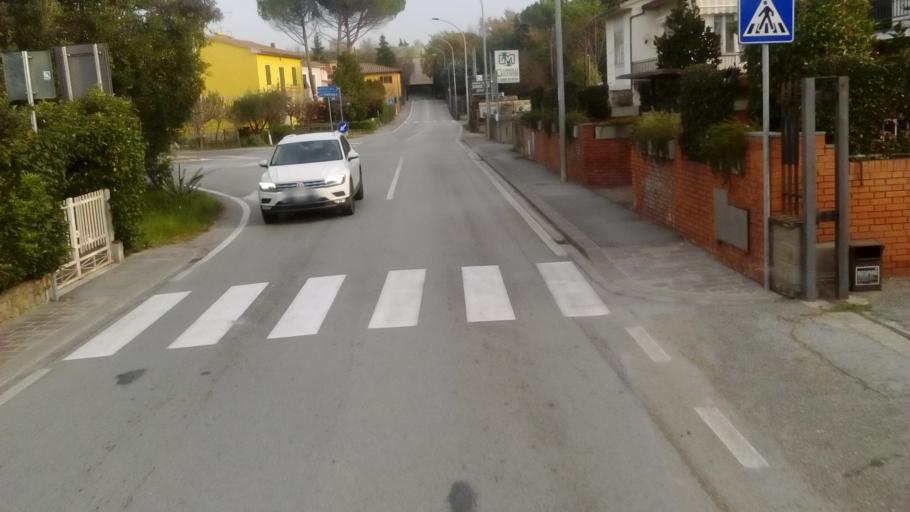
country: IT
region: Tuscany
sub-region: Province of Florence
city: Montelupo Fiorentino
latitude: 43.7206
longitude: 11.0085
